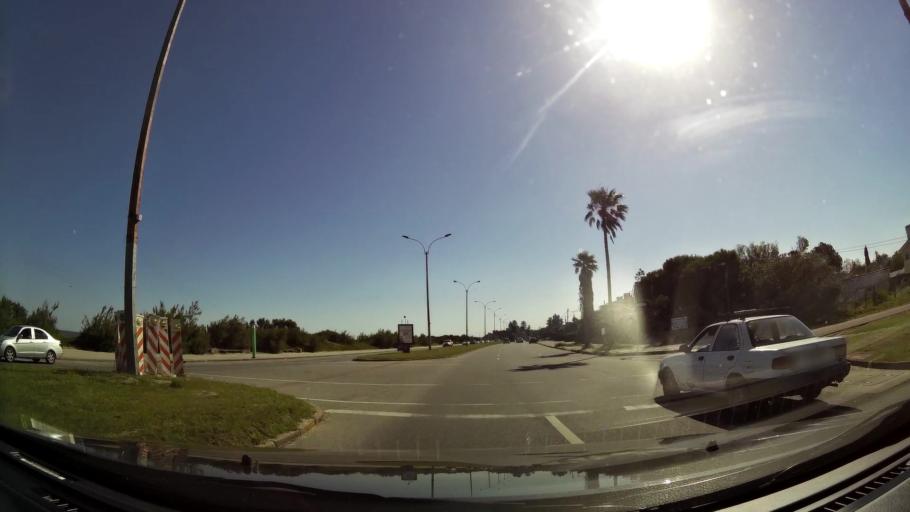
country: UY
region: Canelones
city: Barra de Carrasco
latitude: -34.8867
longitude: -56.0450
